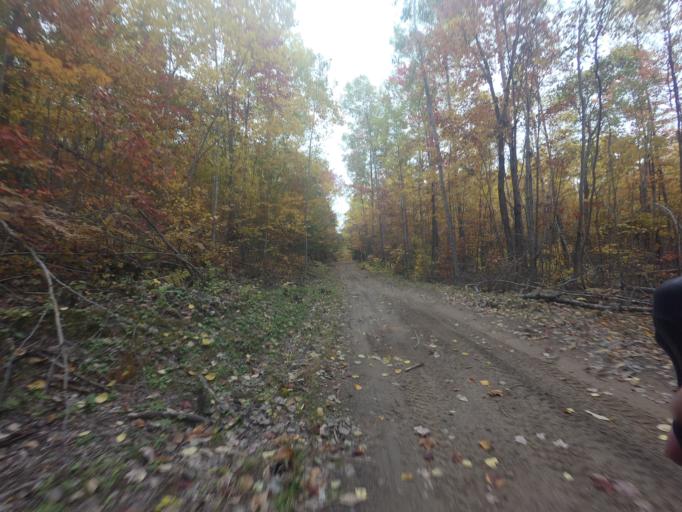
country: CA
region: Ontario
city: Petawawa
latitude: 45.7529
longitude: -77.3568
